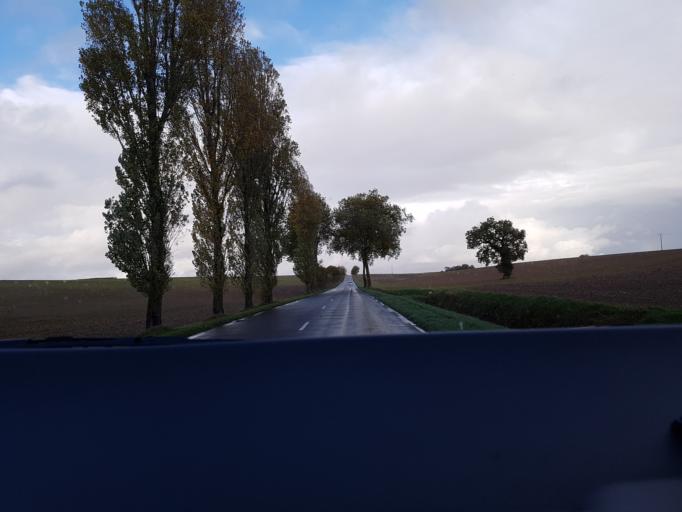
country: FR
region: Poitou-Charentes
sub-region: Departement de la Charente-Maritime
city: Aulnay
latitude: 46.0071
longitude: -0.3835
